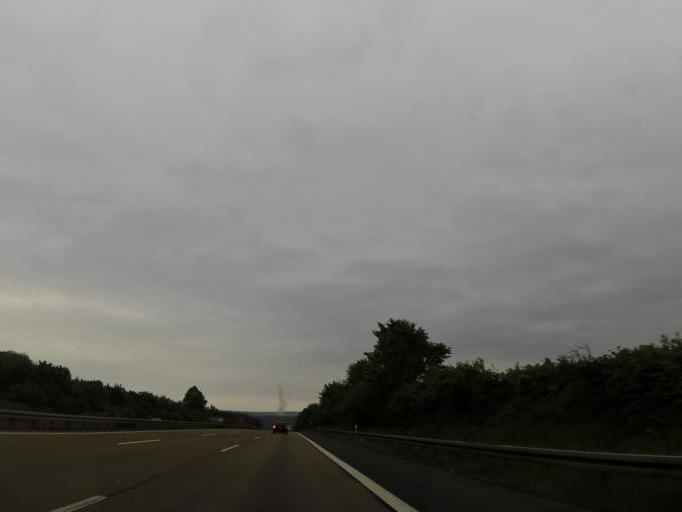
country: DE
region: Hesse
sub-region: Regierungsbezirk Kassel
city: Malsfeld
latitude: 51.0682
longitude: 9.4918
